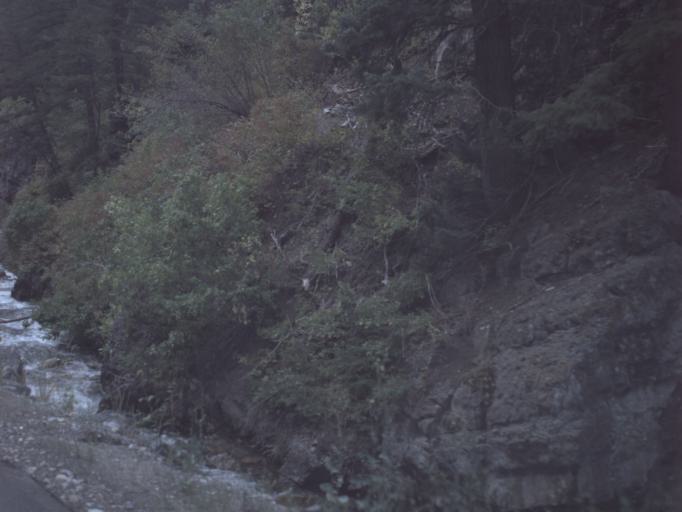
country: US
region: Utah
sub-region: Utah County
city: Orem
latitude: 40.3889
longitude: -111.5744
